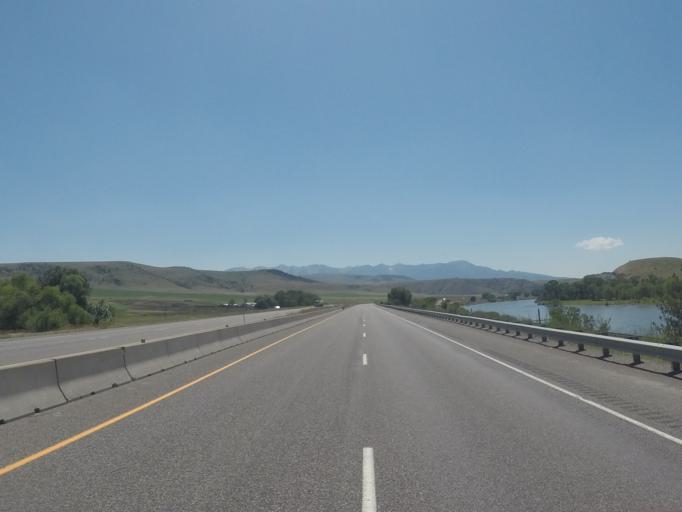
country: US
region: Montana
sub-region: Sweet Grass County
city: Big Timber
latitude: 45.7297
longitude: -110.2364
